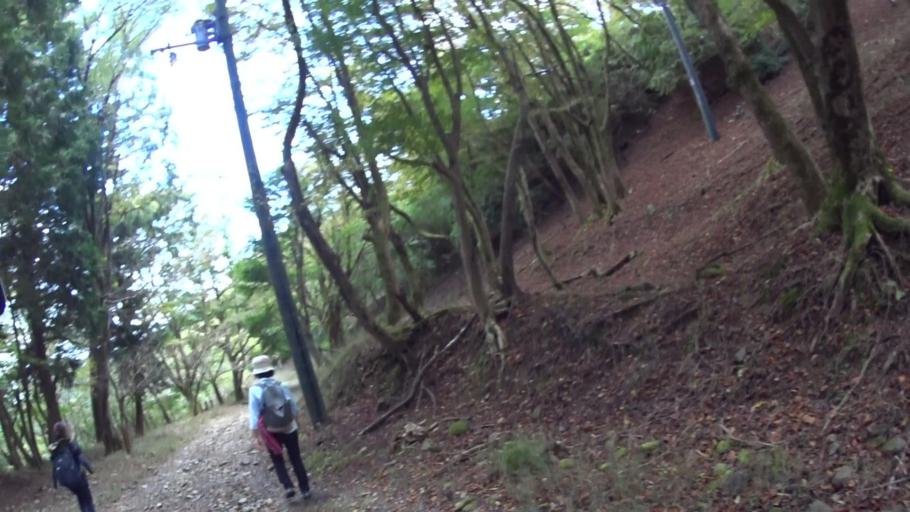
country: JP
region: Shiga Prefecture
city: Otsu-shi
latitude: 35.0677
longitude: 135.8306
